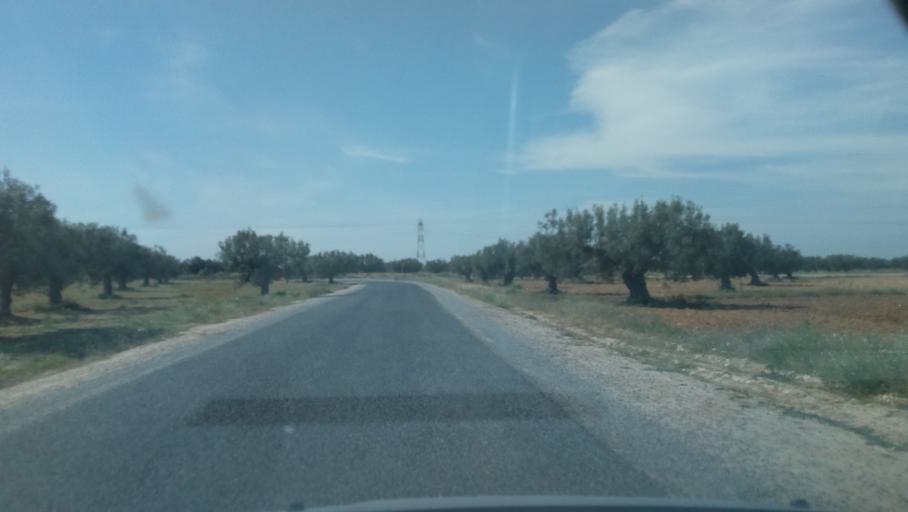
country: TN
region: Safaqis
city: Al Qarmadah
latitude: 34.8778
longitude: 10.8699
